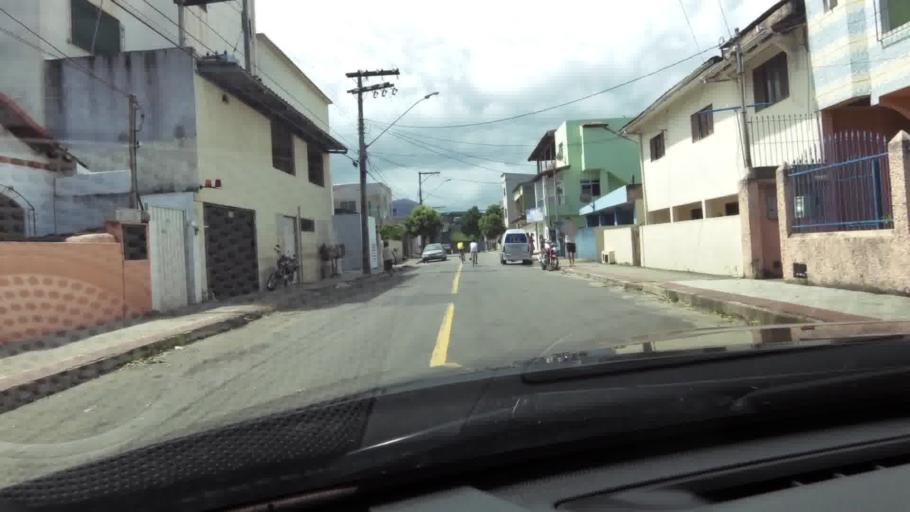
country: BR
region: Espirito Santo
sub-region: Guarapari
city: Guarapari
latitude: -20.6588
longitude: -40.5016
